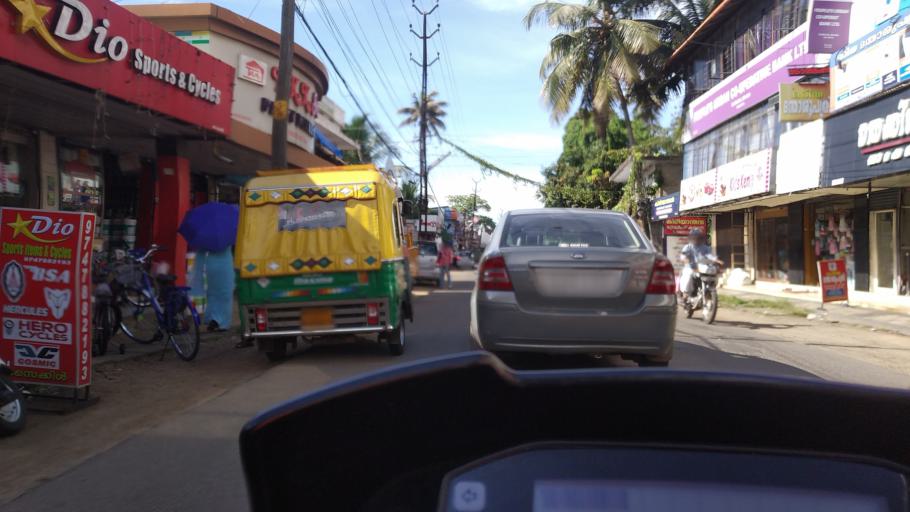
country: IN
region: Kerala
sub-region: Ernakulam
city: Elur
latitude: 10.0457
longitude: 76.2176
